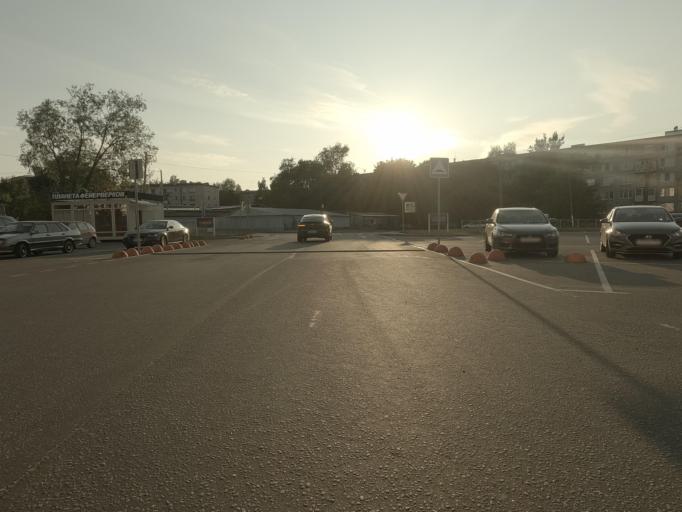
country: RU
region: Leningrad
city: Vyborg
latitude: 60.7078
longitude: 28.7720
